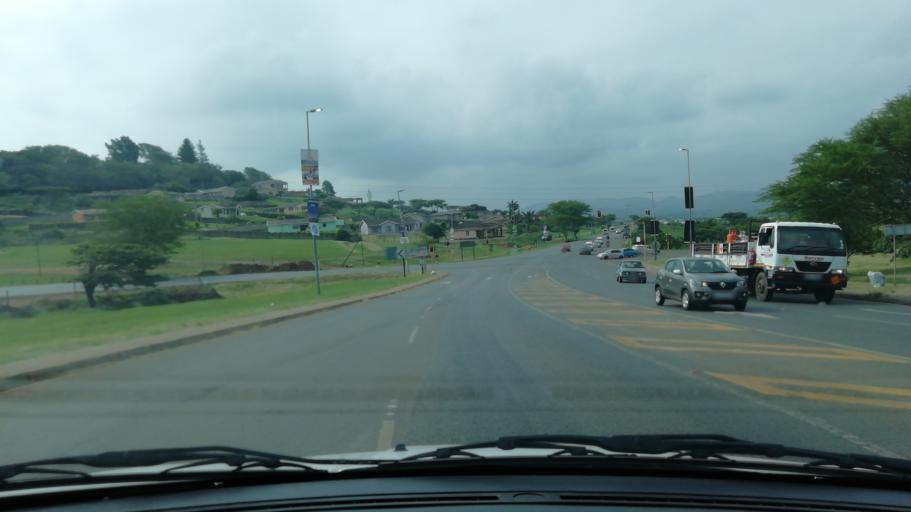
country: ZA
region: KwaZulu-Natal
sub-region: uThungulu District Municipality
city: Empangeni
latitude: -28.7426
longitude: 31.8827
